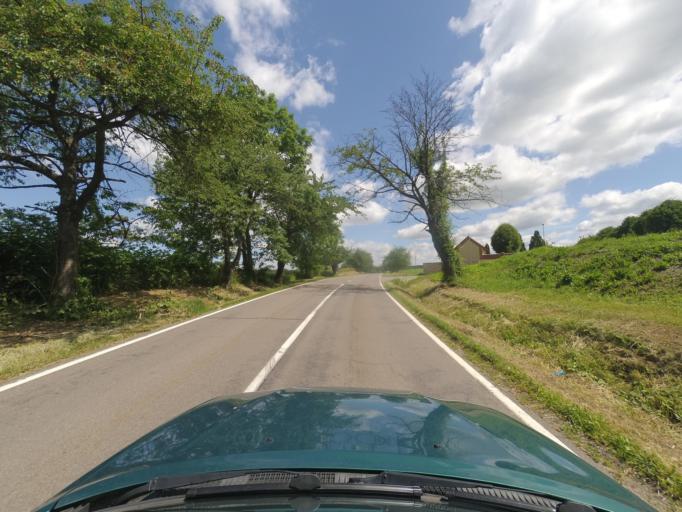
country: CZ
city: Dobruska
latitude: 50.2979
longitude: 16.1698
